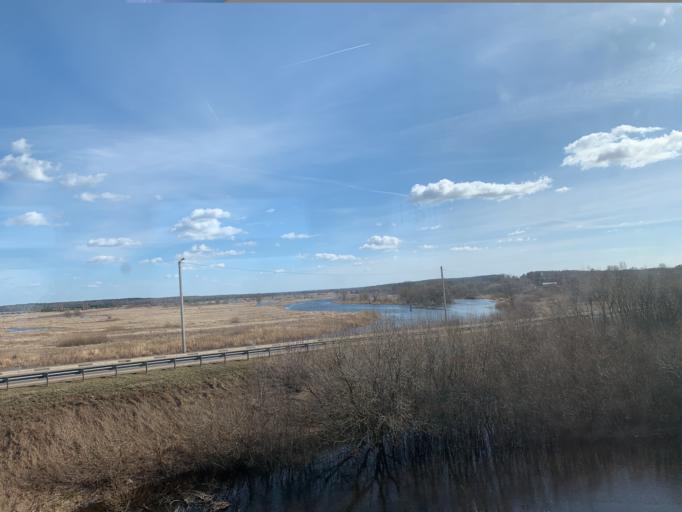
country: BY
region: Minsk
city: Novy Svyerzhan'
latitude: 53.4648
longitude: 26.7272
